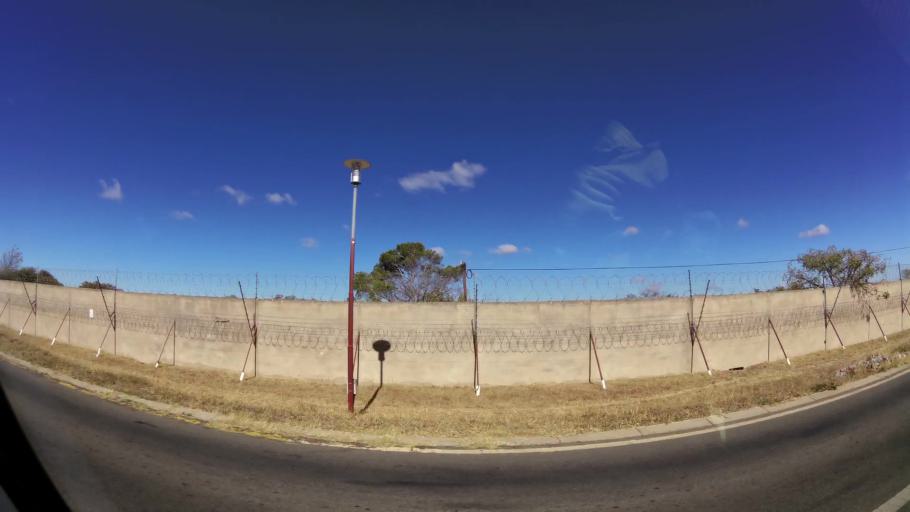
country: ZA
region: Limpopo
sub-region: Capricorn District Municipality
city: Polokwane
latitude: -23.8637
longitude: 29.4570
